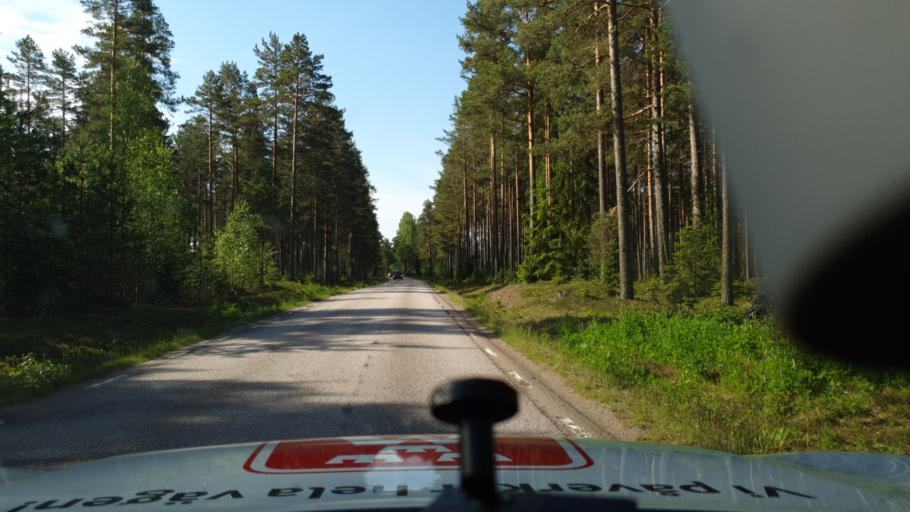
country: SE
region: Vaermland
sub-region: Torsby Kommun
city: Torsby
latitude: 59.9532
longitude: 12.9111
